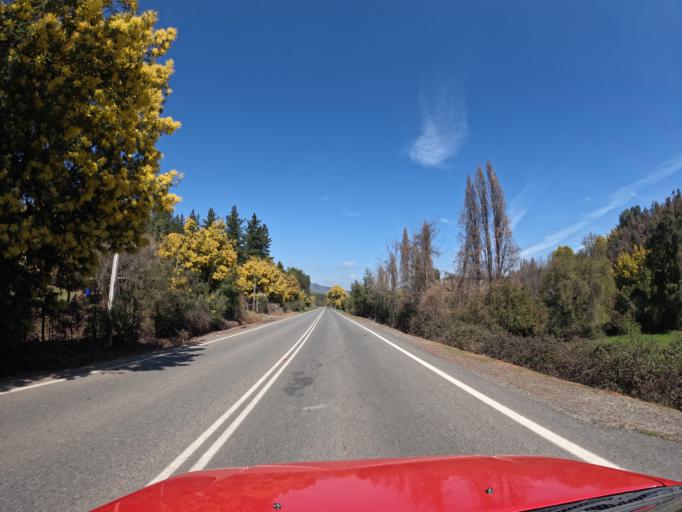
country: CL
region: Maule
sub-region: Provincia de Talca
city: San Clemente
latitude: -35.4587
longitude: -71.2697
